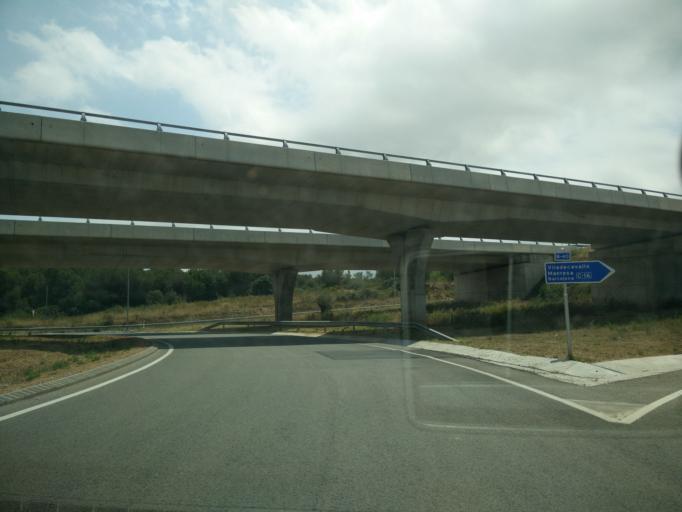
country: ES
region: Catalonia
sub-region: Provincia de Barcelona
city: Terrassa
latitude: 41.5834
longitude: 1.9918
